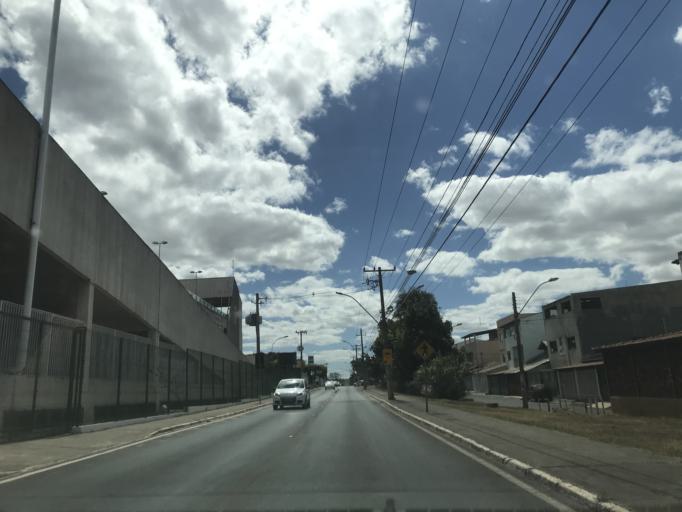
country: BR
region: Federal District
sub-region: Brasilia
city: Brasilia
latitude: -15.8530
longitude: -47.9543
